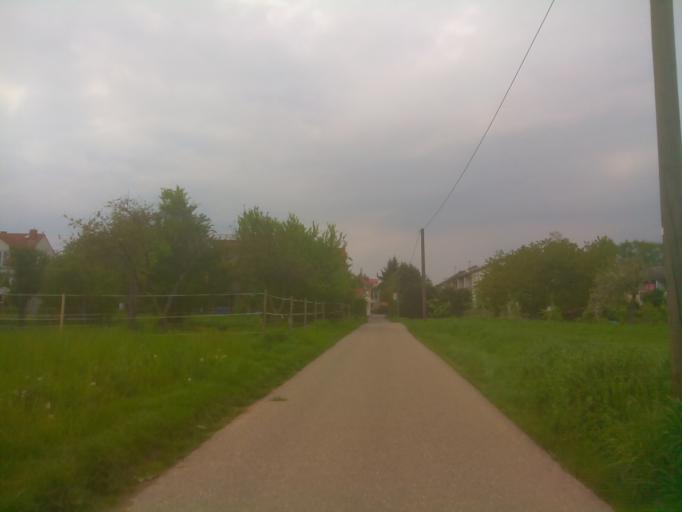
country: DE
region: Baden-Wuerttemberg
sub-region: Karlsruhe Region
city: Schriesheim
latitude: 49.4678
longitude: 8.6550
